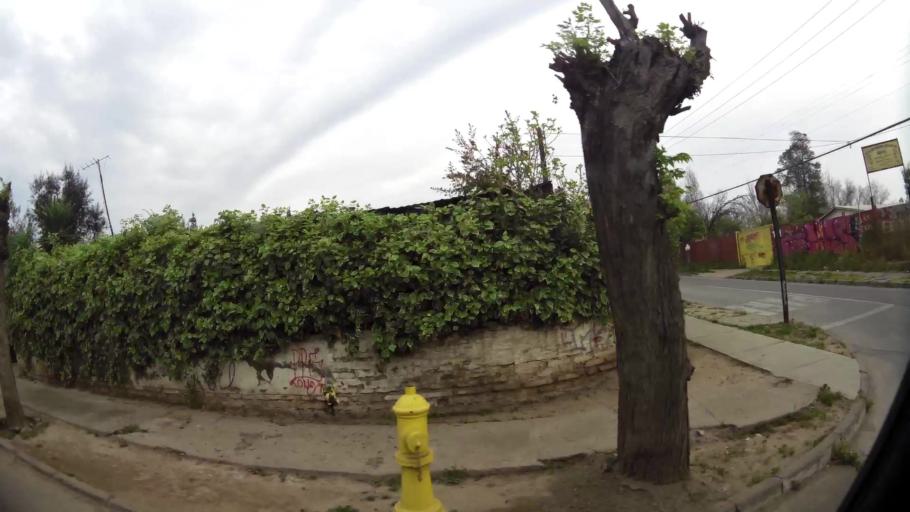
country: CL
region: Santiago Metropolitan
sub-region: Provincia de Santiago
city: Lo Prado
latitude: -33.5037
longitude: -70.7659
